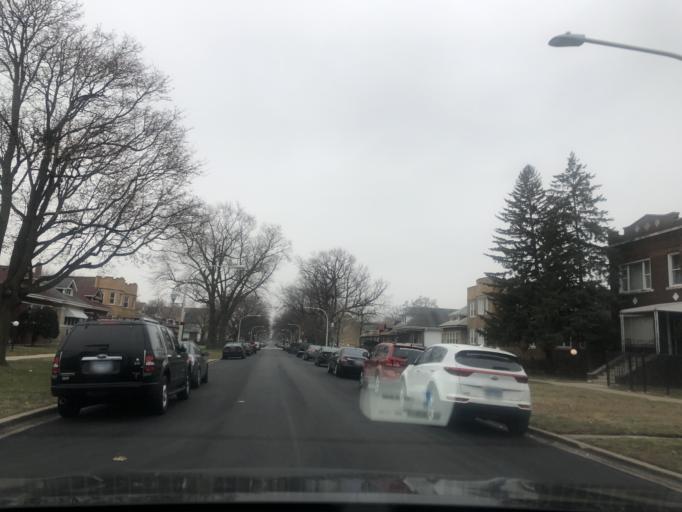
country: US
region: Illinois
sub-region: Cook County
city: Evergreen Park
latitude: 41.7508
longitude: -87.6198
